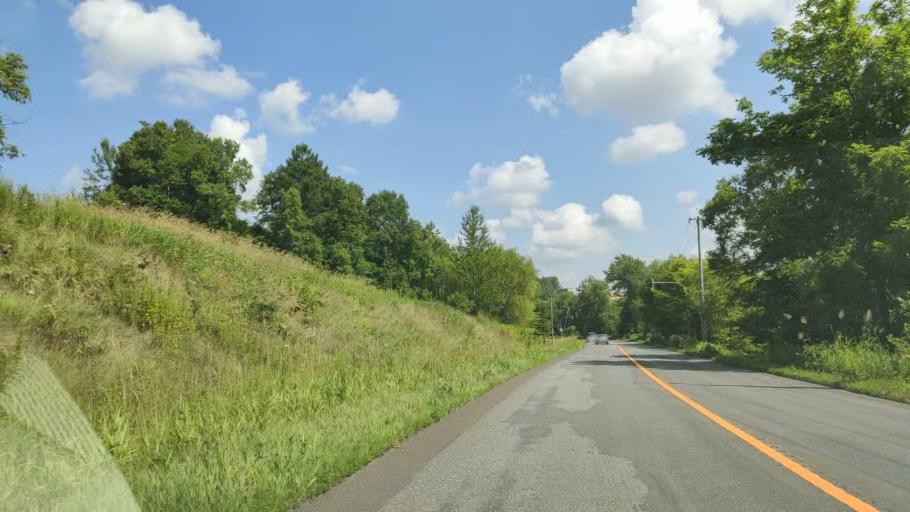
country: JP
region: Hokkaido
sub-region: Asahikawa-shi
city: Asahikawa
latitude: 43.5723
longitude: 142.4381
